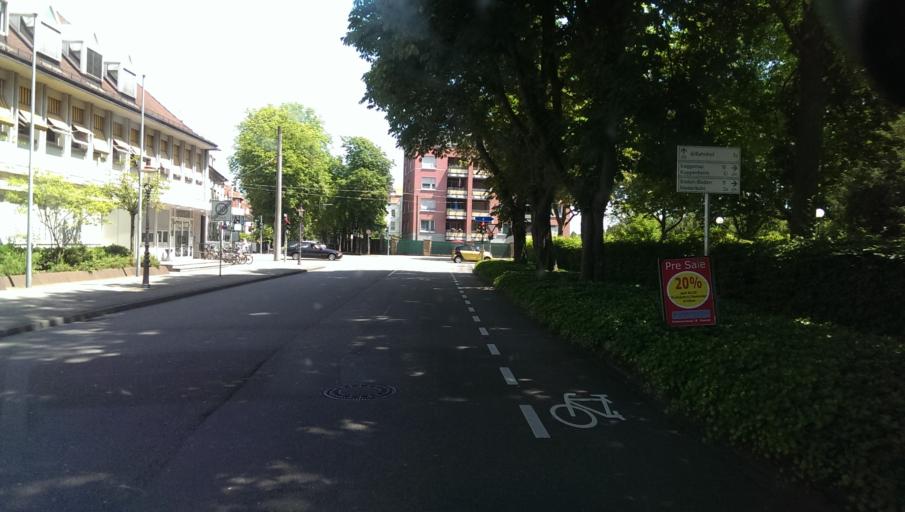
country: DE
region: Baden-Wuerttemberg
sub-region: Karlsruhe Region
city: Rastatt
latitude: 48.8606
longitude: 8.2076
